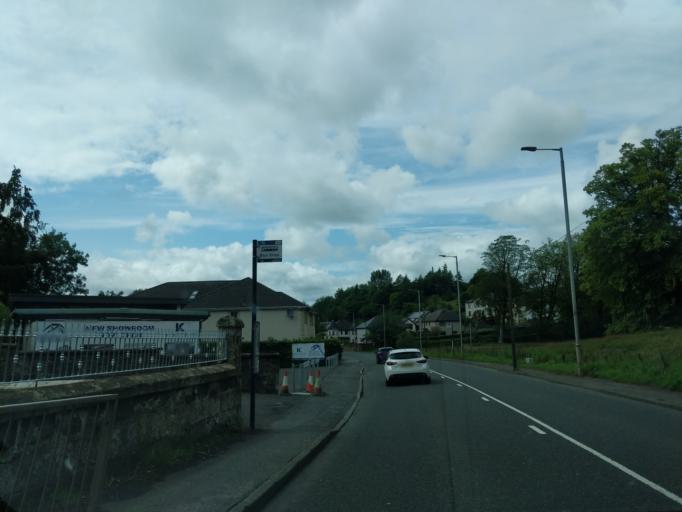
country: GB
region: Scotland
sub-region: South Lanarkshire
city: Strathaven
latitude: 55.6767
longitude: -4.0579
